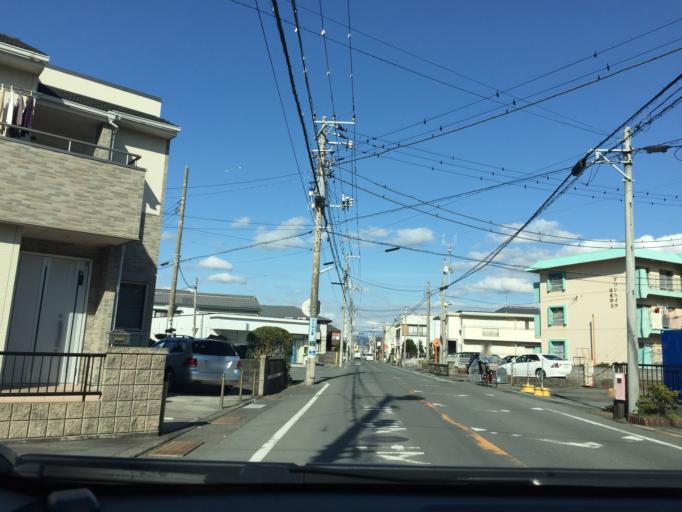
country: JP
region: Shizuoka
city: Numazu
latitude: 35.0767
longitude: 138.8633
